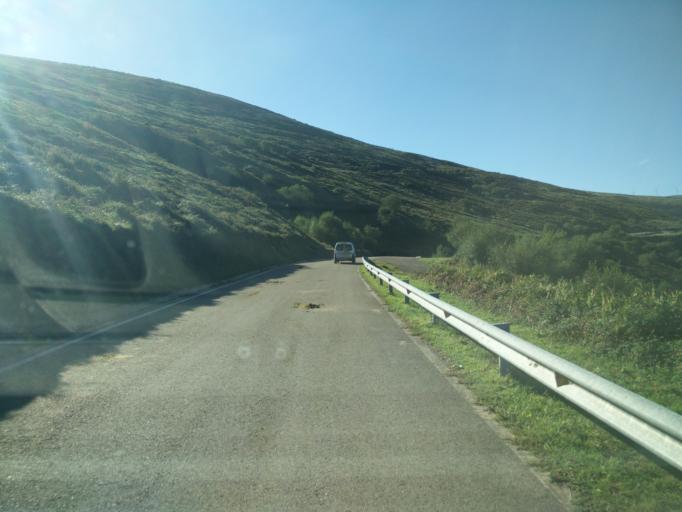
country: ES
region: Cantabria
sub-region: Provincia de Cantabria
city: San Pedro del Romeral
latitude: 43.0944
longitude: -3.8177
